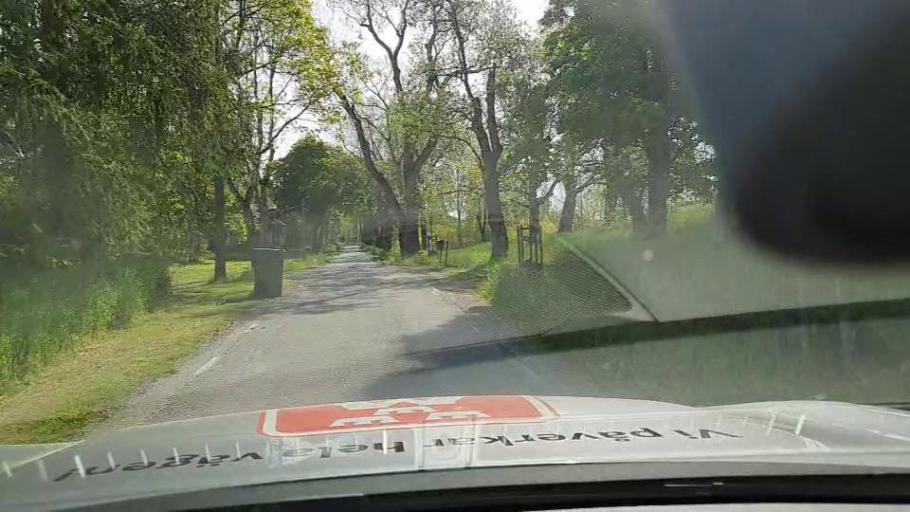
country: SE
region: Soedermanland
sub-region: Eskilstuna Kommun
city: Arla
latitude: 59.2582
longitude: 16.6625
